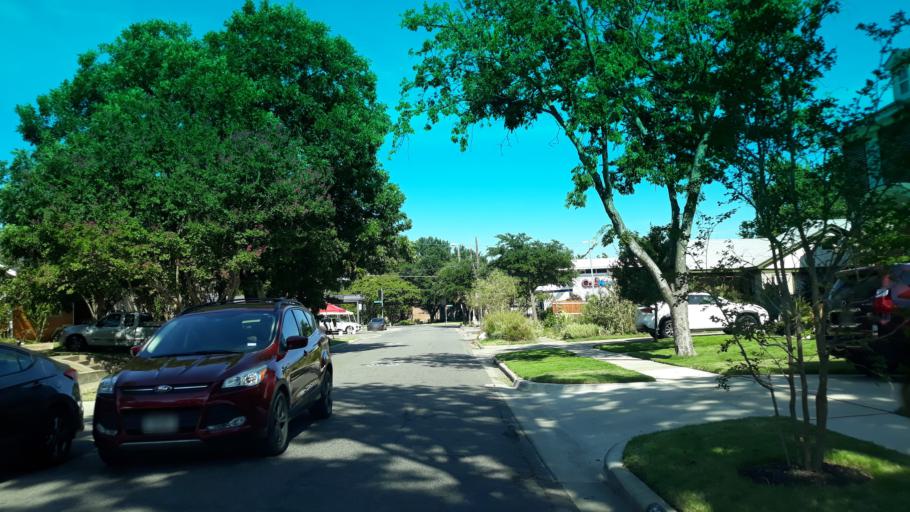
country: US
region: Texas
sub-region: Dallas County
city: Highland Park
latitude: 32.8172
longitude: -96.7541
